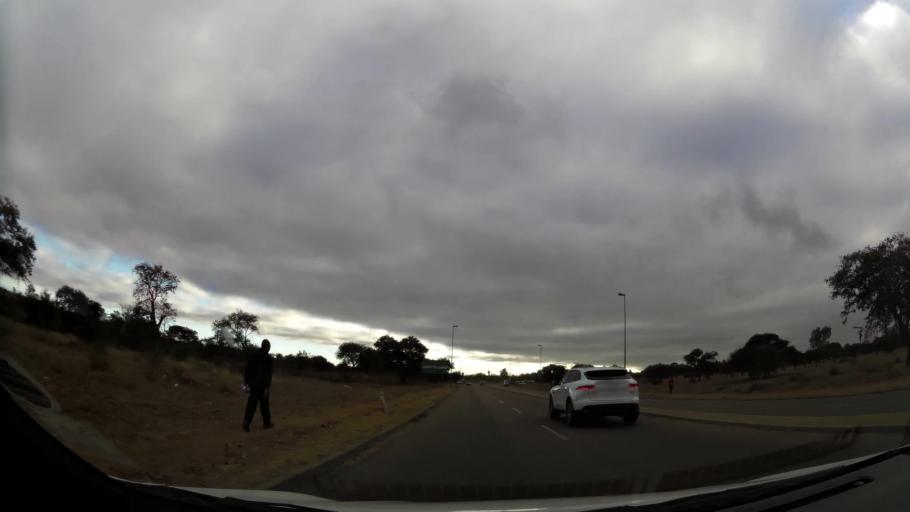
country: ZA
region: Limpopo
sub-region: Capricorn District Municipality
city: Polokwane
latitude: -23.8843
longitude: 29.4318
